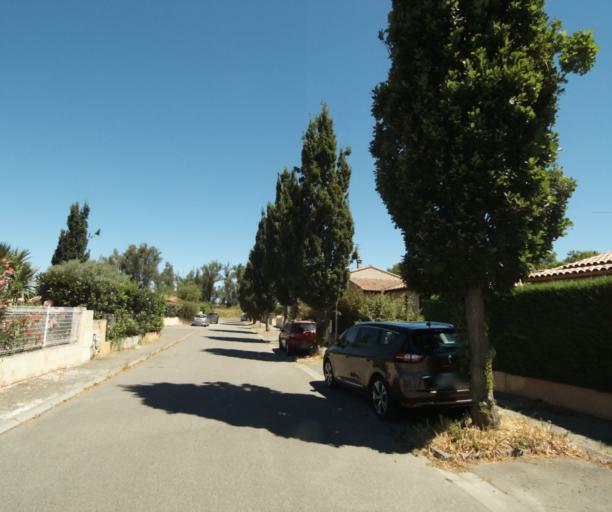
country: FR
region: Midi-Pyrenees
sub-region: Departement de la Haute-Garonne
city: Pechabou
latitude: 43.5136
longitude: 1.5143
